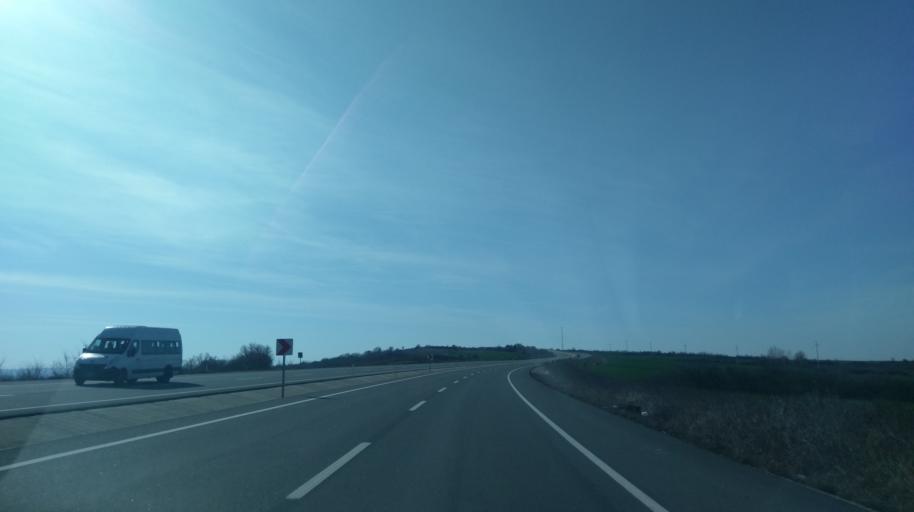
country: TR
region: Edirne
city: Hamidiye
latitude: 41.0918
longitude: 26.6409
